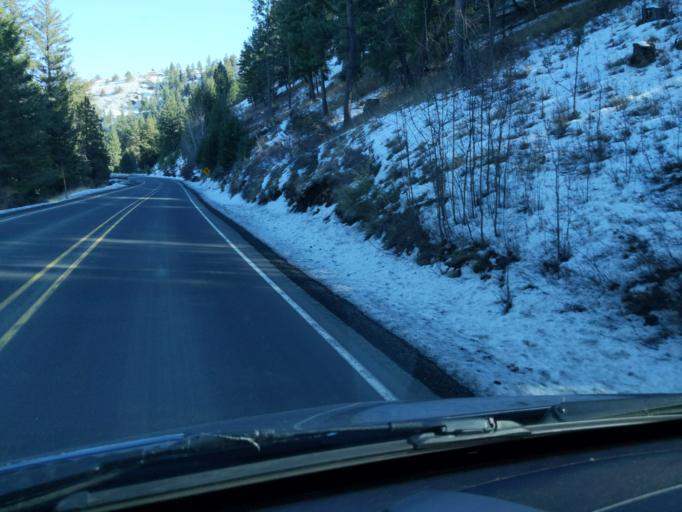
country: US
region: Oregon
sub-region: Grant County
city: John Day
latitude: 44.8361
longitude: -119.0360
